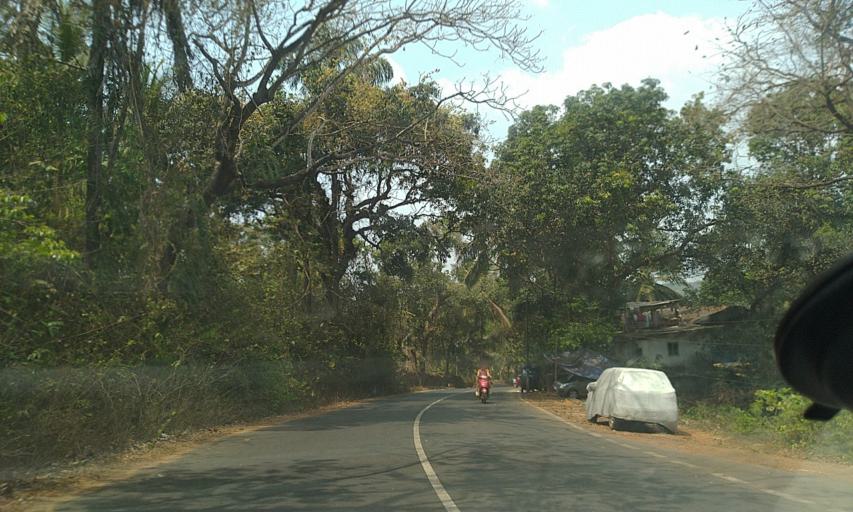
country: IN
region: Goa
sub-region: North Goa
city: Pernem
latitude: 15.7115
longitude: 73.7981
